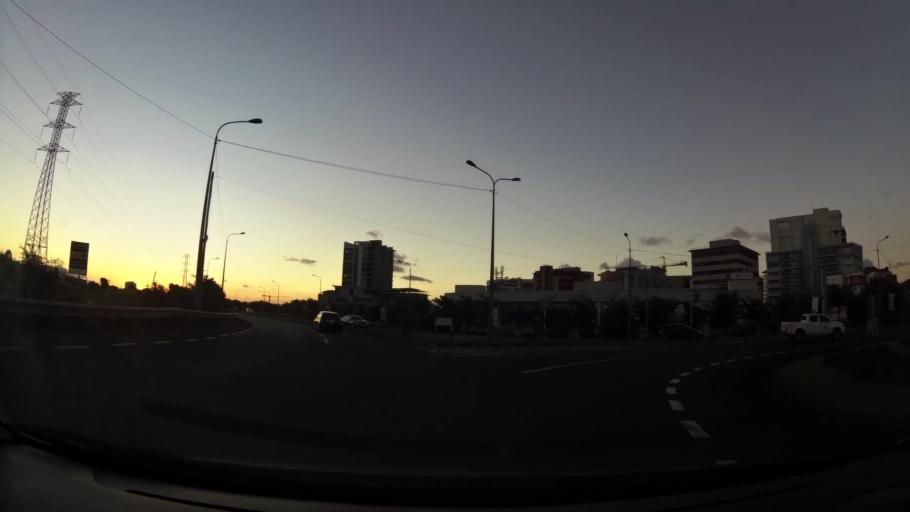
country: MU
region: Plaines Wilhems
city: Ebene
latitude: -20.2472
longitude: 57.4894
